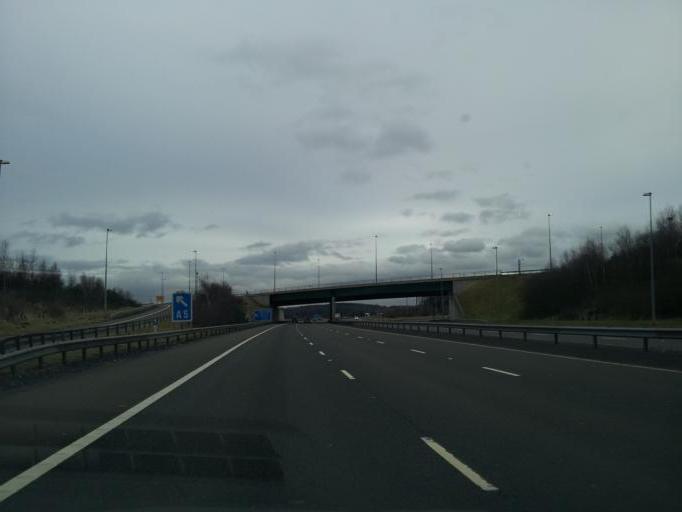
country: GB
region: England
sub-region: Staffordshire
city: Shenstone
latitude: 52.6405
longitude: -1.8146
